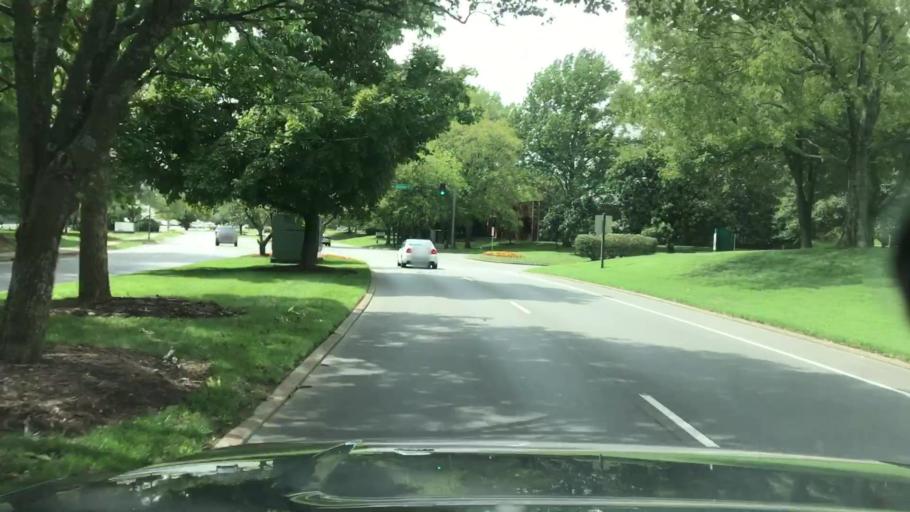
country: US
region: Tennessee
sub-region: Williamson County
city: Brentwood
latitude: 36.0342
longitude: -86.7944
